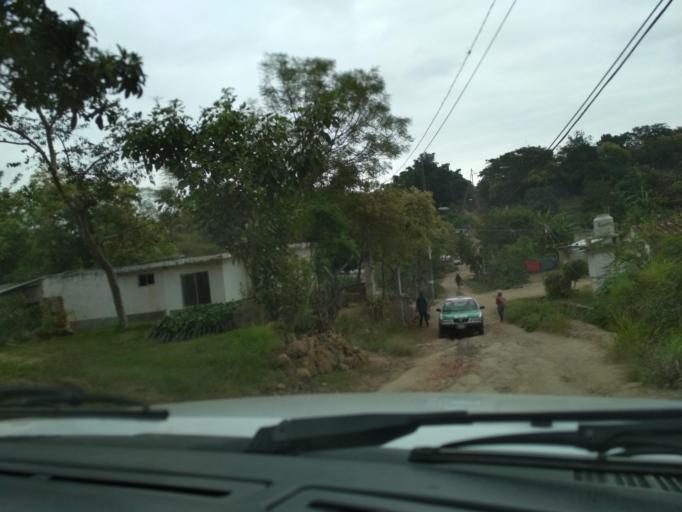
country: MX
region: Veracruz
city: El Castillo
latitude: 19.5794
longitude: -96.8658
